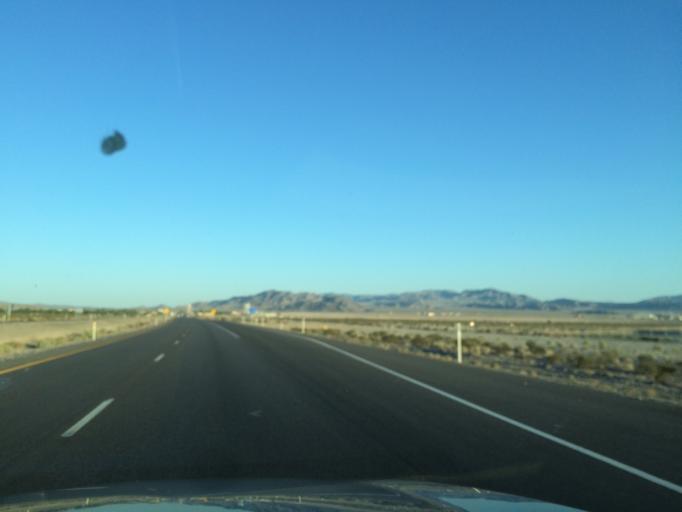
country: US
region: Nevada
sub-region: Nye County
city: Pahrump
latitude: 36.5767
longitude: -115.6464
